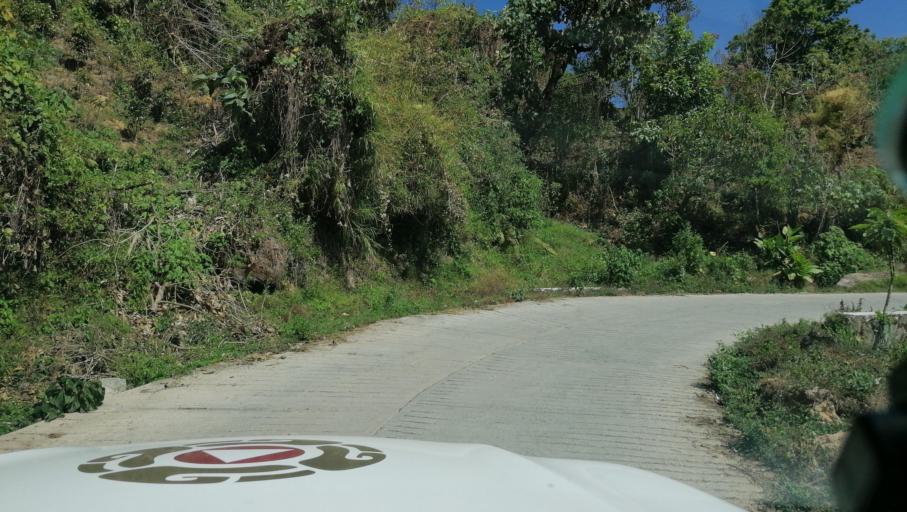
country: GT
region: San Marcos
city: Tacana
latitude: 15.2023
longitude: -92.2065
